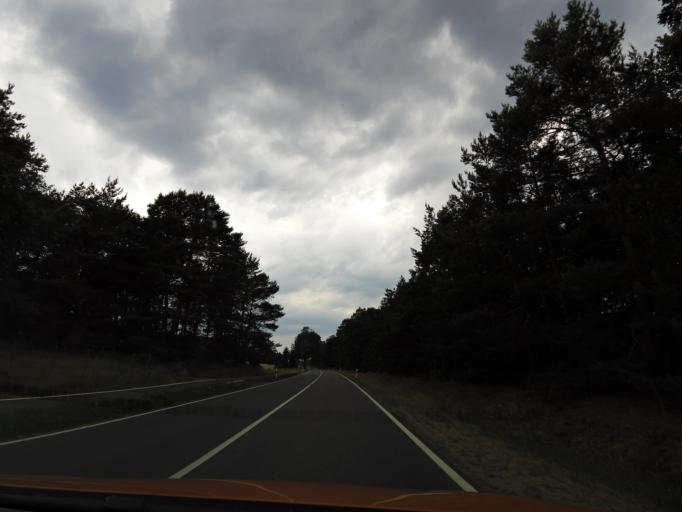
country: DE
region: Brandenburg
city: Baruth
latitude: 52.0378
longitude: 13.5183
